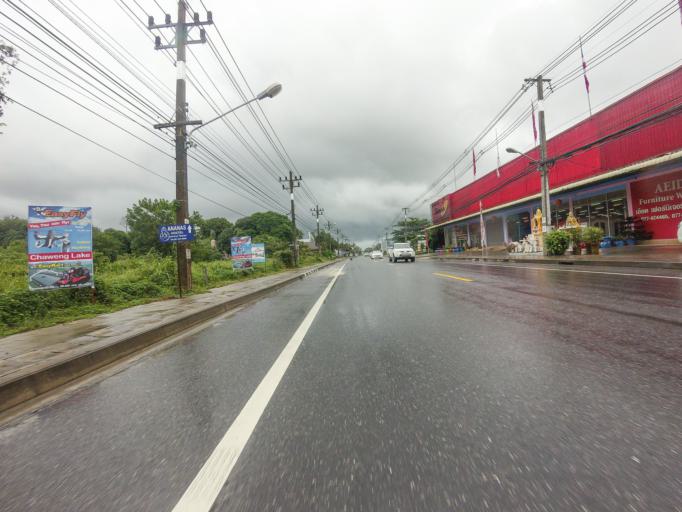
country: TH
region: Surat Thani
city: Ko Samui
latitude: 9.4550
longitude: 99.9948
